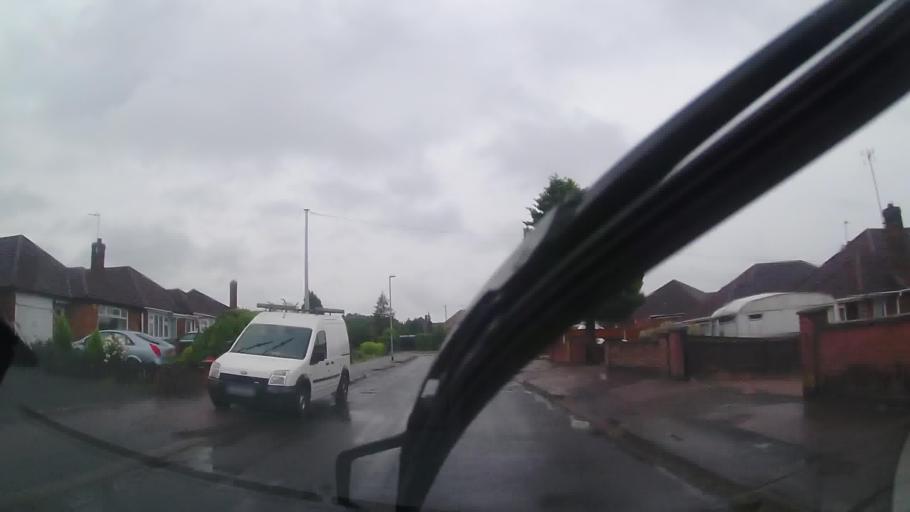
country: GB
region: England
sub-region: Leicestershire
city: Glenfield
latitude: 52.6476
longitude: -1.1930
